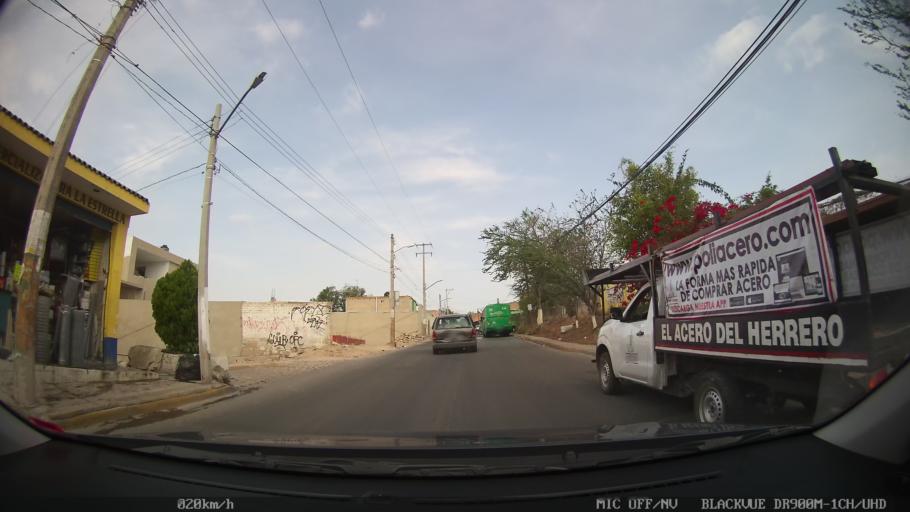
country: MX
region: Jalisco
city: Tonala
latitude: 20.6203
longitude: -103.2328
